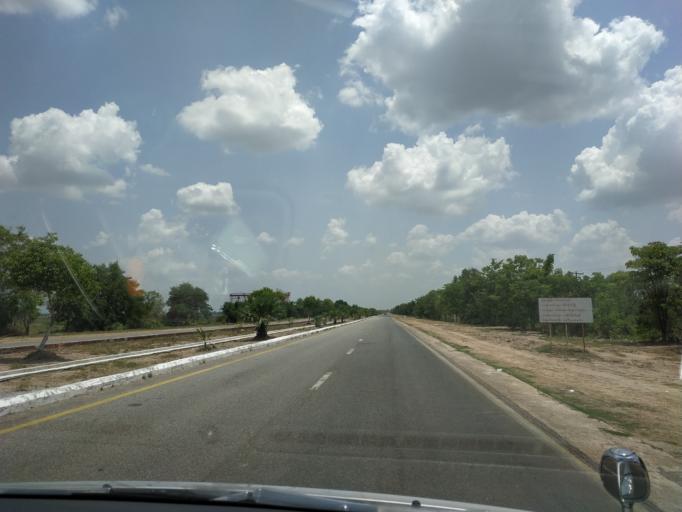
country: MM
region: Bago
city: Thanatpin
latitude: 17.0859
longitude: 96.1755
